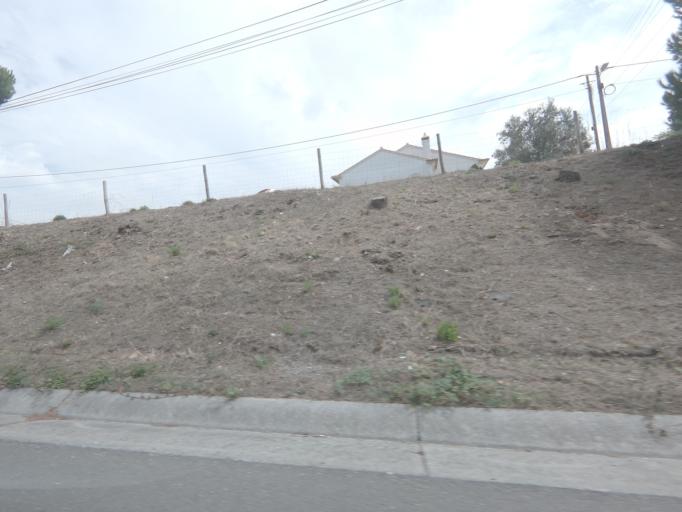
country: PT
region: Leiria
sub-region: Leiria
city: Leiria
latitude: 39.7580
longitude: -8.8103
